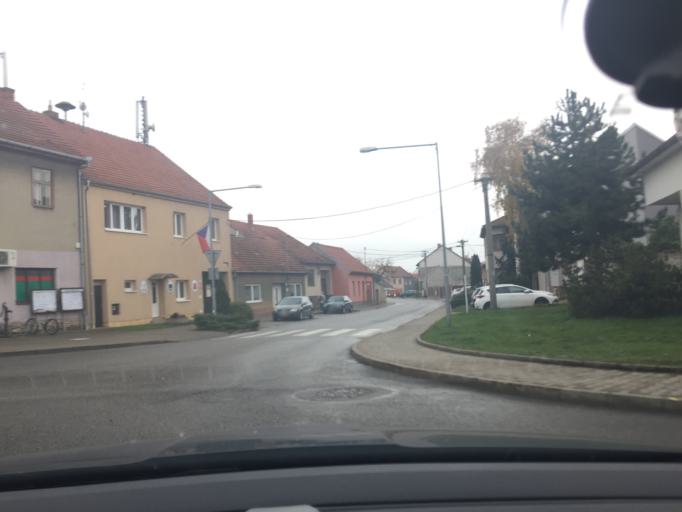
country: CZ
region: South Moravian
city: Blazovice
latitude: 49.1413
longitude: 16.7657
